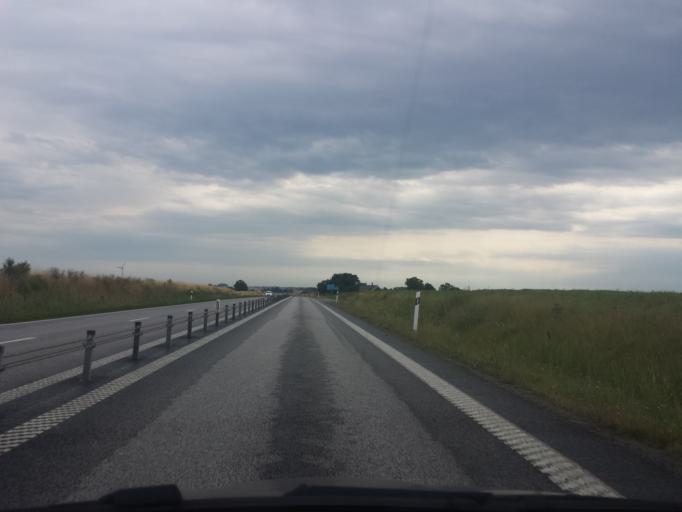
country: SE
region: Skane
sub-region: Skurups Kommun
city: Rydsgard
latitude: 55.4771
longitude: 13.6394
